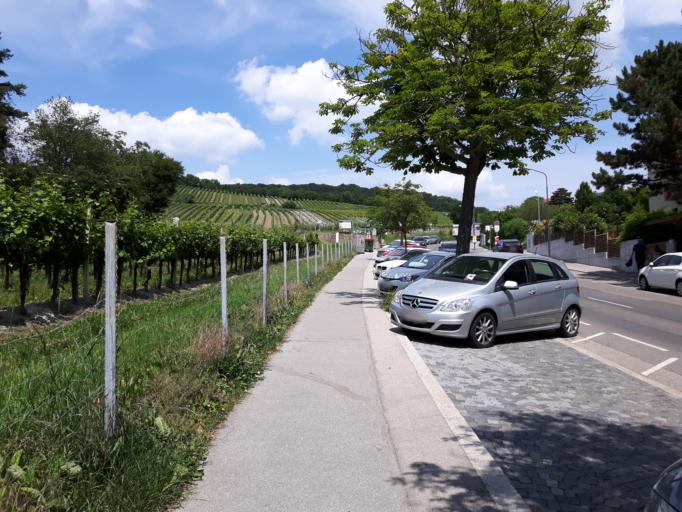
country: AT
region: Lower Austria
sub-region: Politischer Bezirk Wien-Umgebung
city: Klosterneuburg
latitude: 48.2520
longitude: 16.3078
